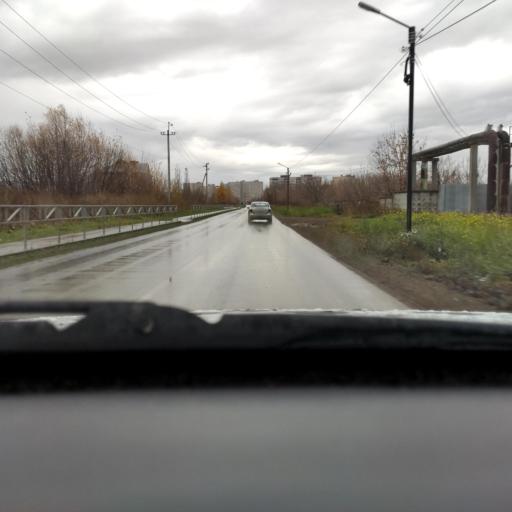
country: RU
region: Perm
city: Kondratovo
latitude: 57.9831
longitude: 56.1153
